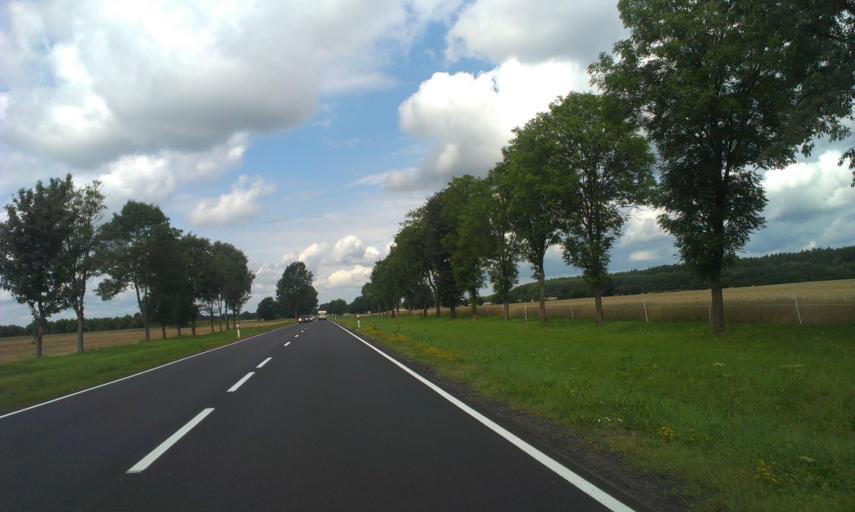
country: PL
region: West Pomeranian Voivodeship
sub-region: Powiat koszalinski
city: Bobolice
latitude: 54.0176
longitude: 16.4885
